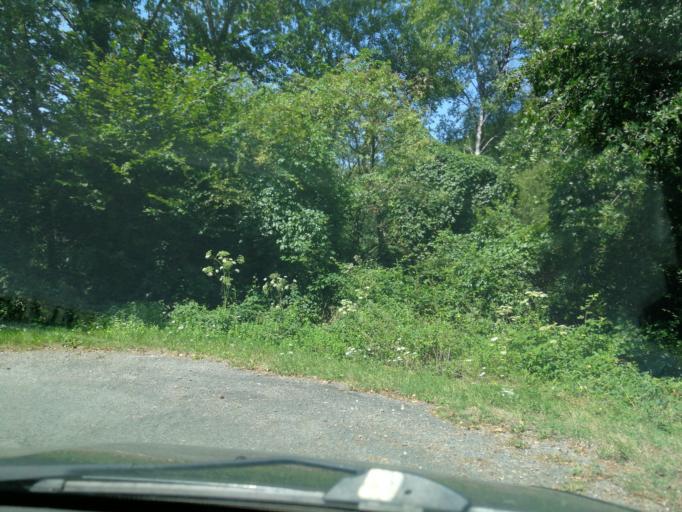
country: FR
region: Auvergne
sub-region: Departement du Cantal
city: Maurs
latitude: 44.6849
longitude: 2.3276
